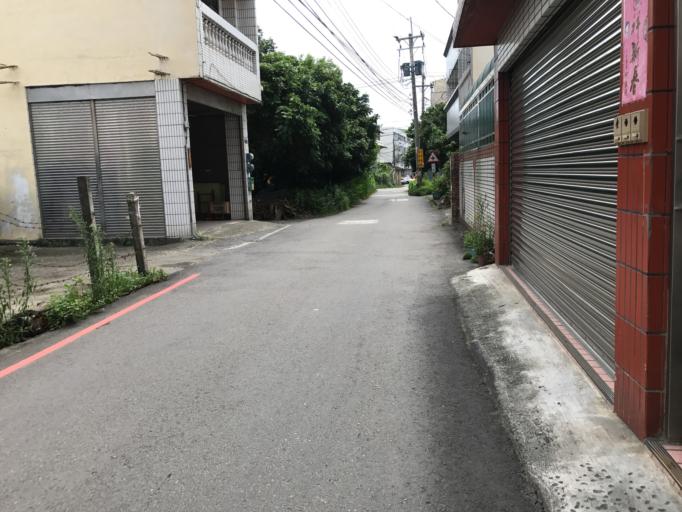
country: TW
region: Taiwan
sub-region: Taichung City
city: Taichung
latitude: 24.0784
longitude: 120.7137
